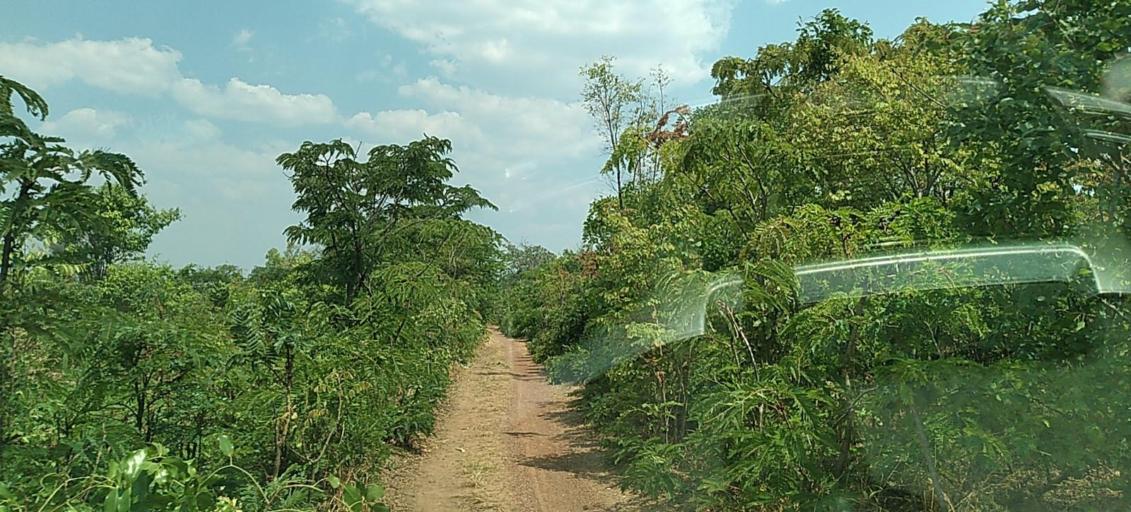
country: CD
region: Katanga
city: Kipushi
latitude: -12.0134
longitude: 27.4330
